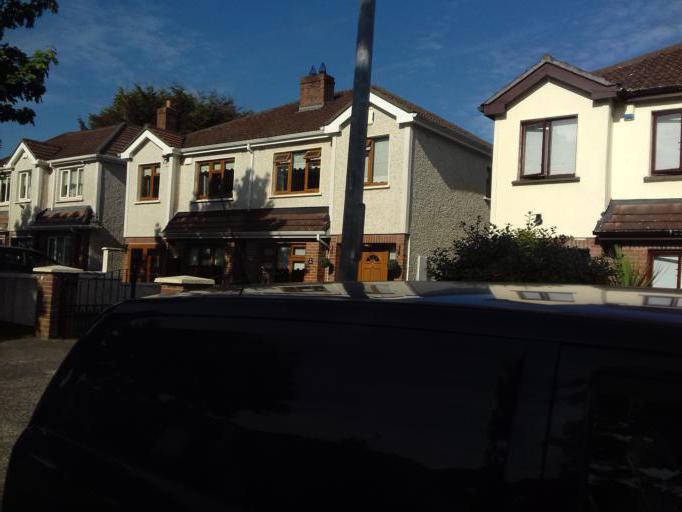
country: IE
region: Leinster
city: Hartstown
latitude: 53.3817
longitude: -6.4109
